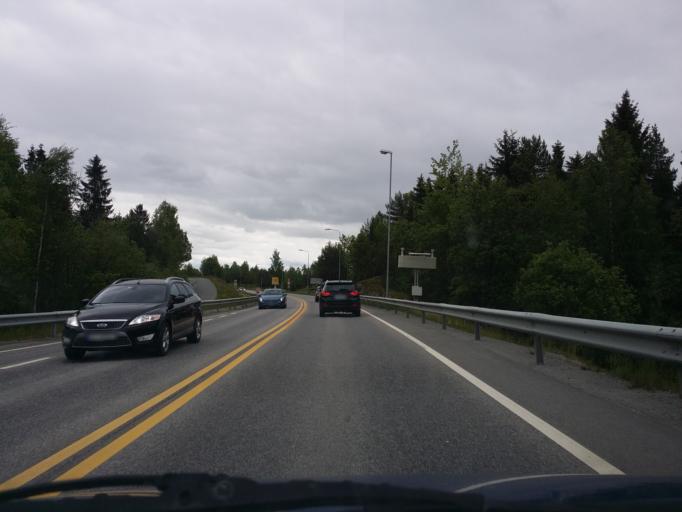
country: NO
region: Hedmark
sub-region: Ringsaker
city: Moelv
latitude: 60.9209
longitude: 10.6959
